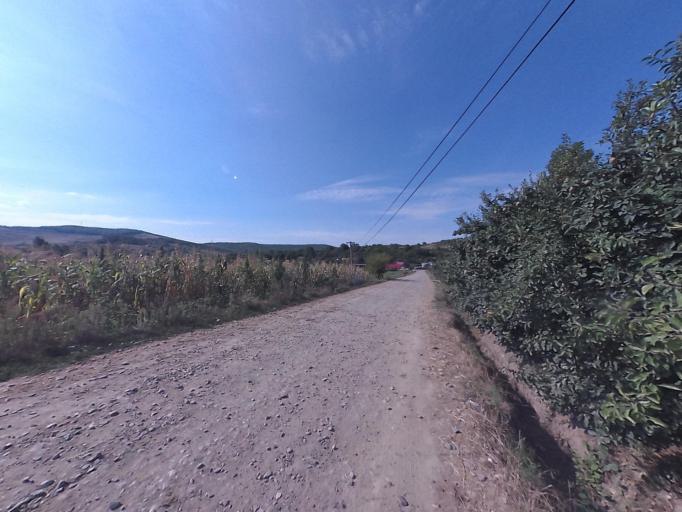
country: RO
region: Vaslui
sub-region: Comuna Osesti
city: Buda
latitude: 46.7615
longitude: 27.4276
